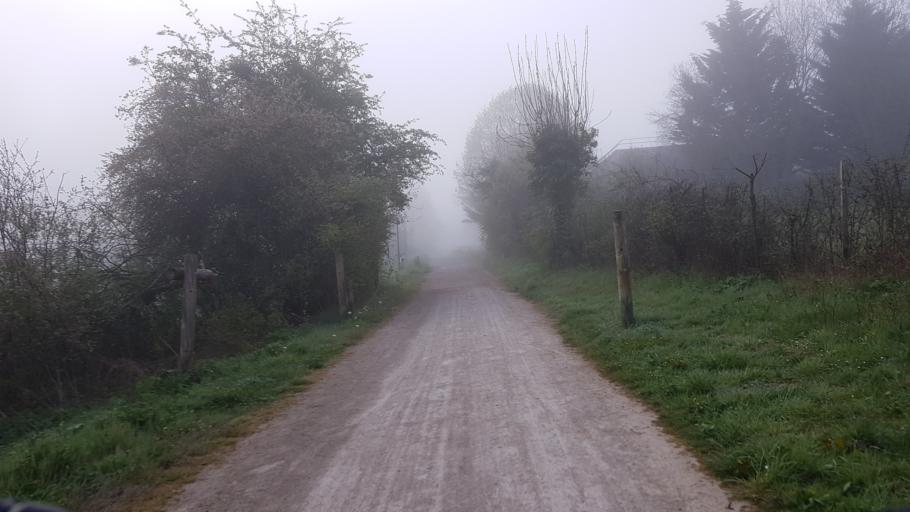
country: FR
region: Ile-de-France
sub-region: Departement des Yvelines
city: Saint-Remy-les-Chevreuse
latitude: 48.7008
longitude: 2.0941
